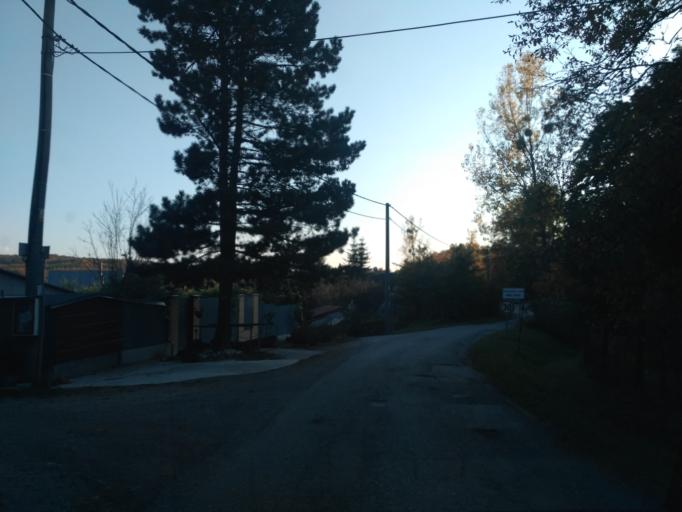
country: SK
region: Kosicky
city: Kosice
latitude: 48.7711
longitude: 21.2890
